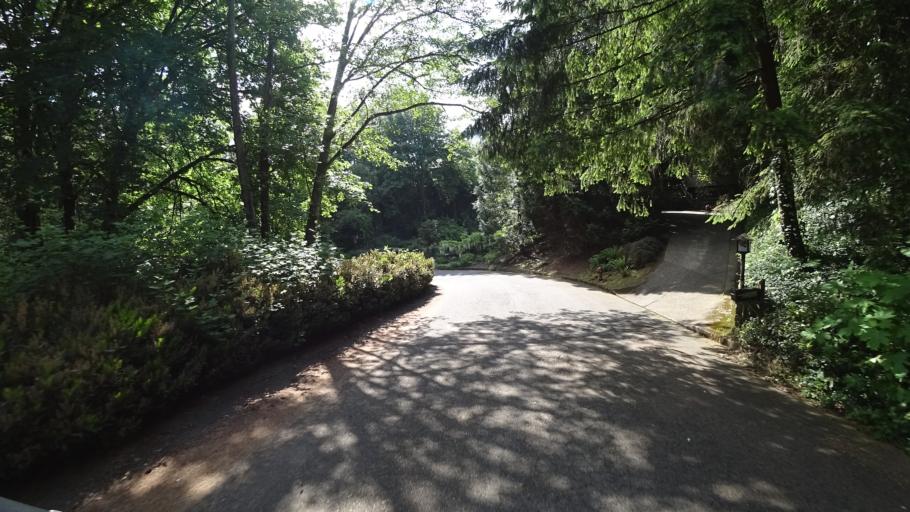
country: US
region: Oregon
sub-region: Washington County
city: West Slope
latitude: 45.5076
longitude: -122.7287
